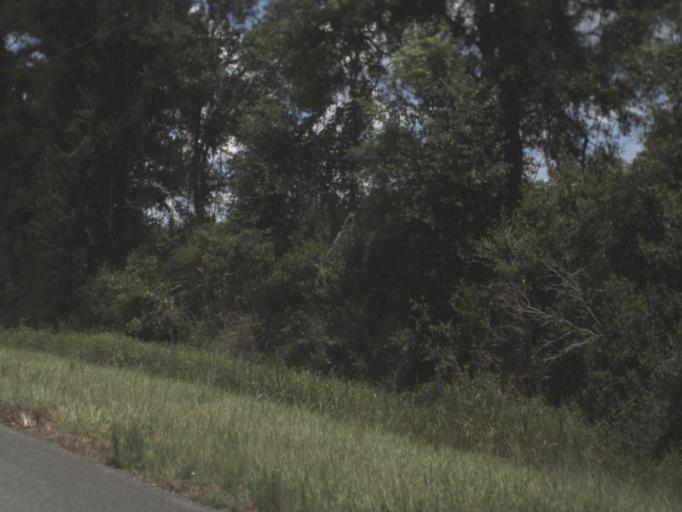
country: US
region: Florida
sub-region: Taylor County
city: Perry
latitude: 30.1000
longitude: -83.6952
